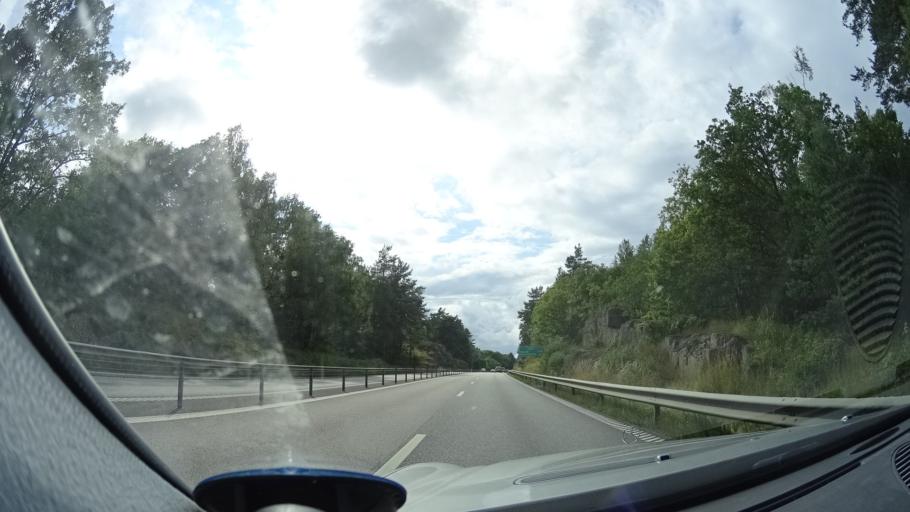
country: SE
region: Blekinge
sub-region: Karlshamns Kommun
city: Karlshamn
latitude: 56.1875
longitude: 14.8142
